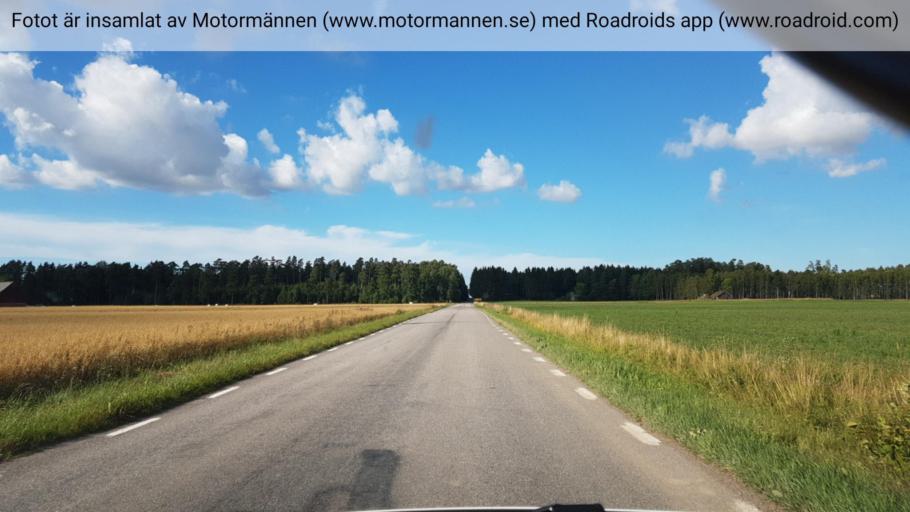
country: SE
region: Vaestra Goetaland
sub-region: Gotene Kommun
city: Kallby
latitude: 58.4498
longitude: 13.3375
